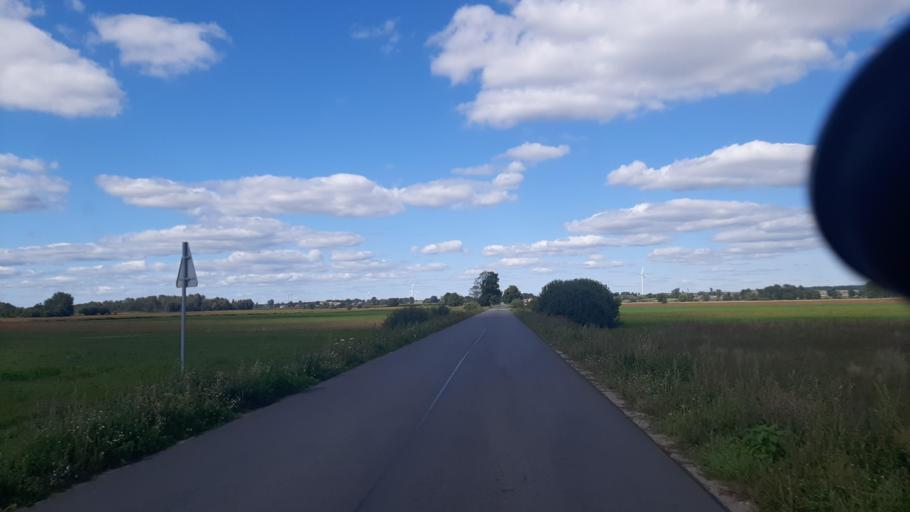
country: PL
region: Lublin Voivodeship
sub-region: Powiat lubartowski
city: Abramow
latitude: 51.4389
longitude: 22.3147
